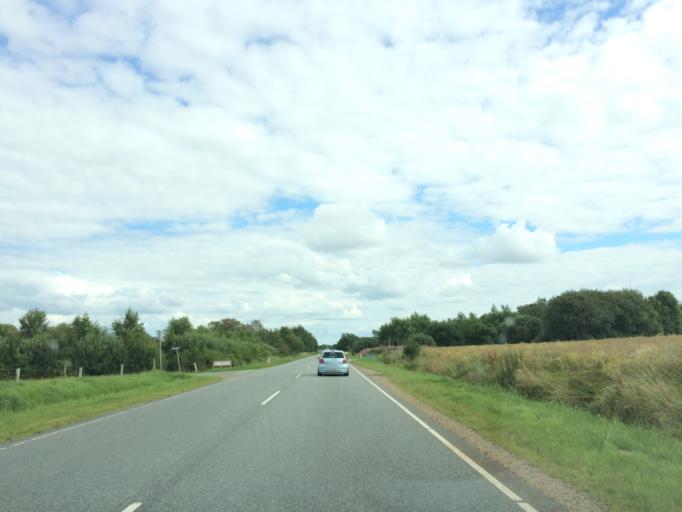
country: DK
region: Central Jutland
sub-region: Favrskov Kommune
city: Hammel
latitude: 56.2643
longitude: 9.7416
